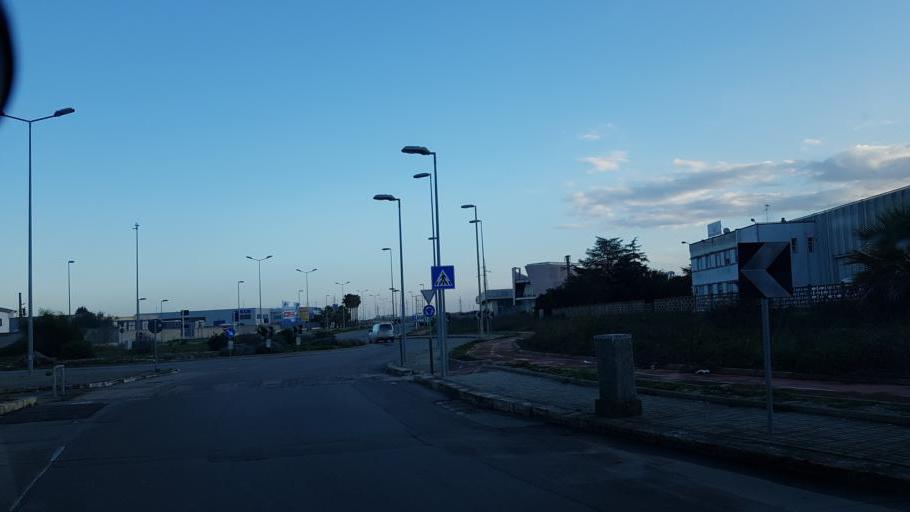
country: IT
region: Apulia
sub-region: Provincia di Lecce
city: Giorgilorio
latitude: 40.3744
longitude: 18.1355
